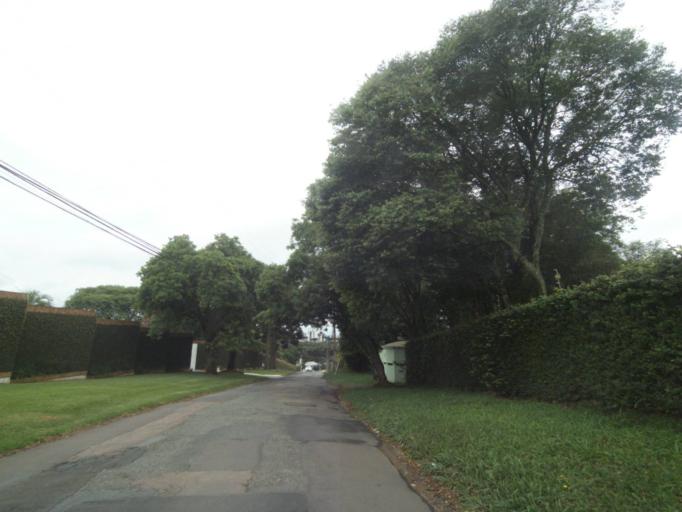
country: BR
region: Parana
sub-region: Curitiba
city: Curitiba
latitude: -25.4512
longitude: -49.3364
